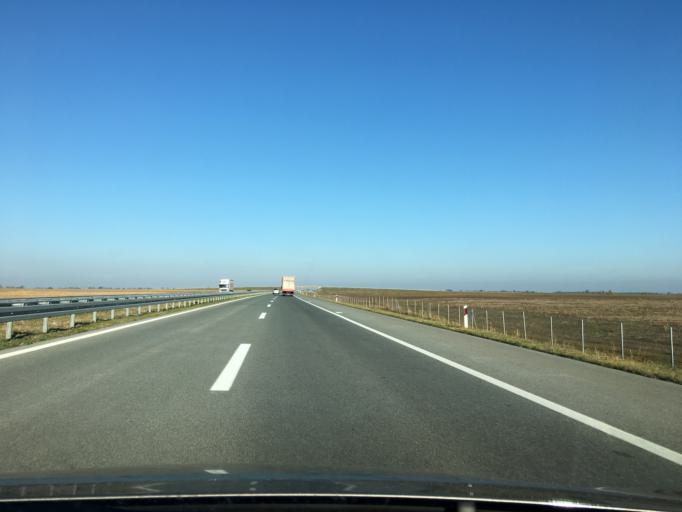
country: RS
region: Autonomna Pokrajina Vojvodina
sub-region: Severnobacki Okrug
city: Mali Igos
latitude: 45.7240
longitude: 19.7080
